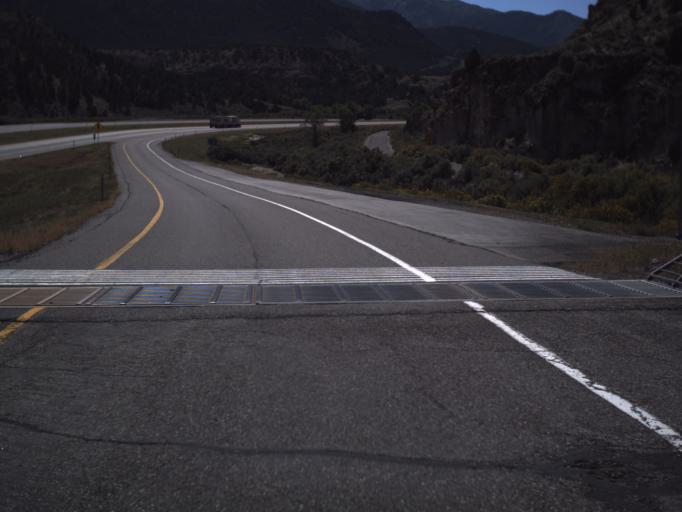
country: US
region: Utah
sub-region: Sevier County
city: Monroe
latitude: 38.5708
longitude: -112.3513
